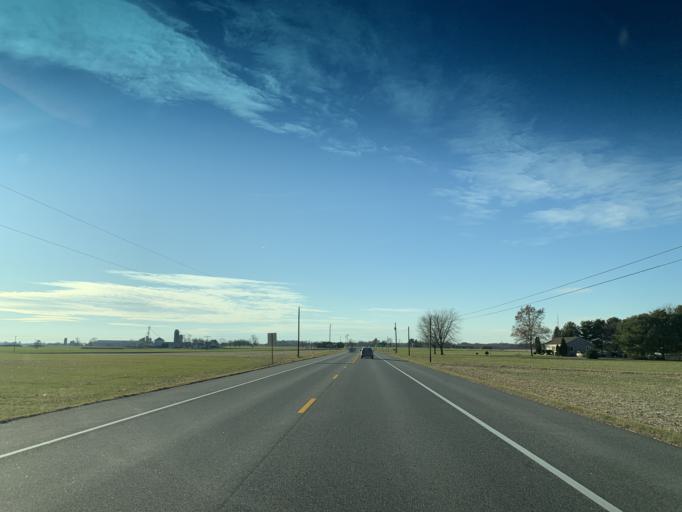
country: US
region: Maryland
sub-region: Queen Anne's County
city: Kingstown
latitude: 39.3273
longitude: -75.9443
